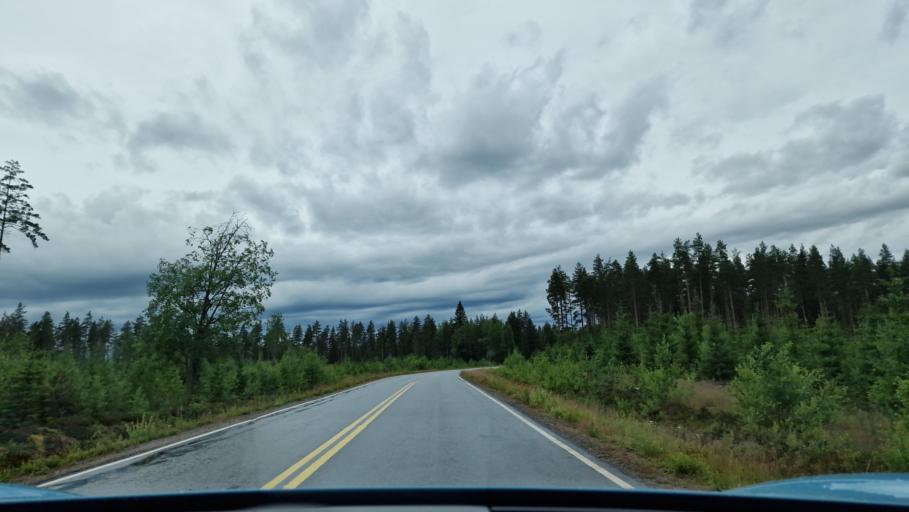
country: FI
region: Central Finland
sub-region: Saarijaervi-Viitasaari
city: Pylkoenmaeki
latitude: 62.6710
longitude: 24.5140
